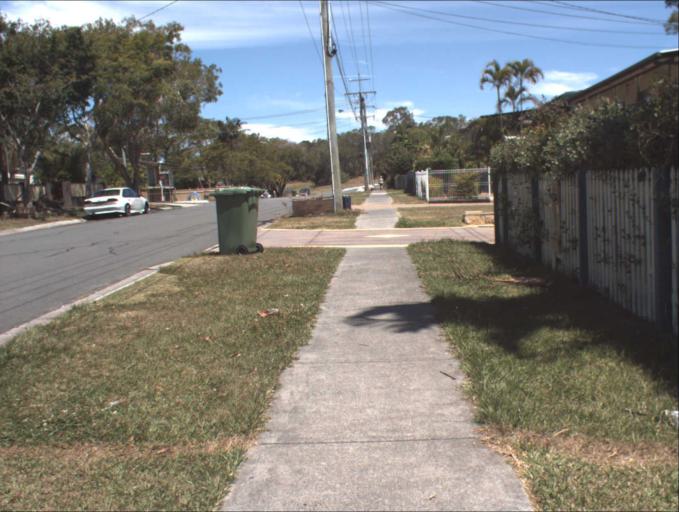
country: AU
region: Queensland
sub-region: Logan
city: Logan City
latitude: -27.6462
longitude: 153.1211
